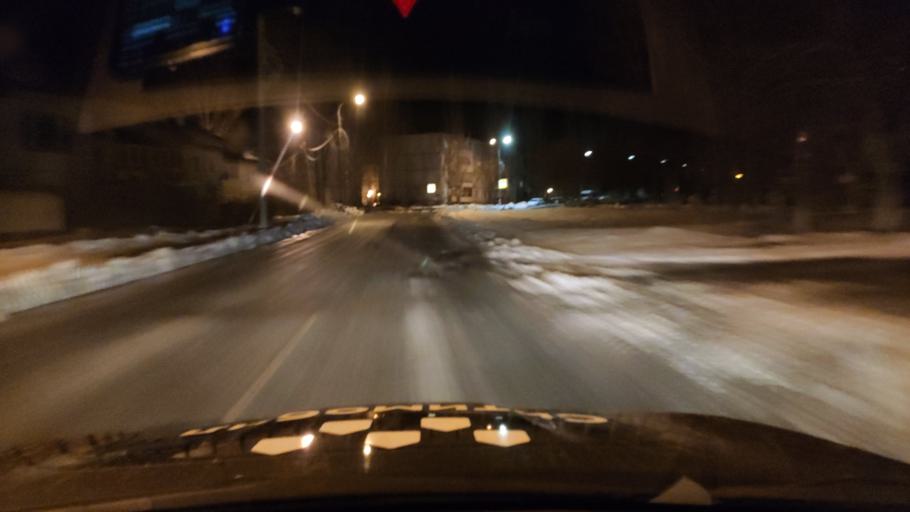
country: RU
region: Samara
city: Povolzhskiy
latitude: 53.5879
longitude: 49.7580
